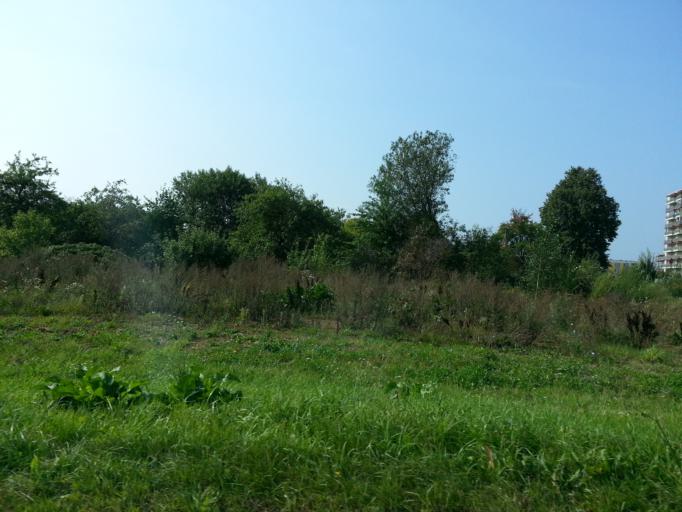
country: LT
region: Vilnius County
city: Pasilaiciai
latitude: 54.7354
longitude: 25.2180
